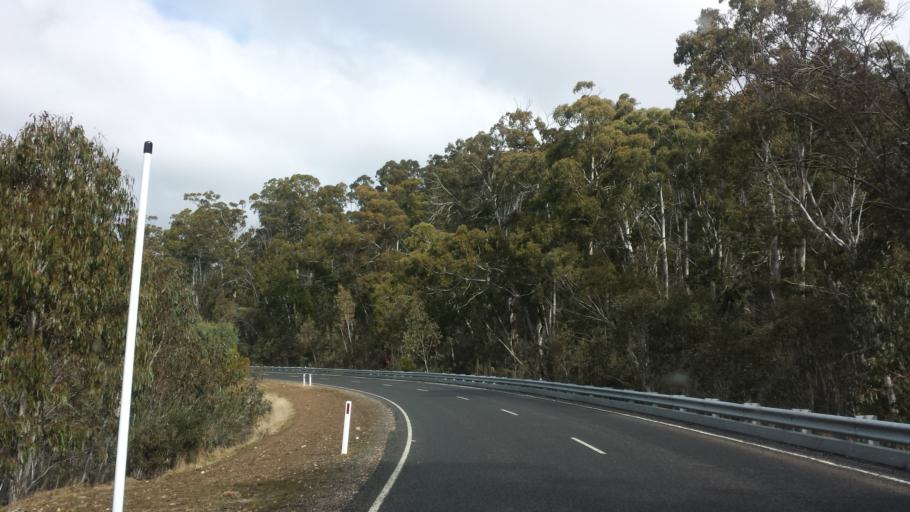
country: AU
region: Victoria
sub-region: Alpine
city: Mount Beauty
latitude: -37.0840
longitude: 147.3860
